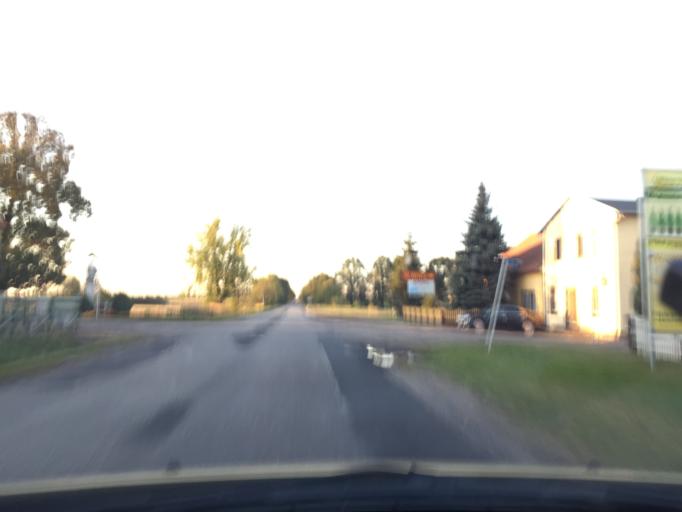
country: PL
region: Greater Poland Voivodeship
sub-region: Powiat pleszewski
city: Dobrzyca
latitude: 51.8413
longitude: 17.6202
